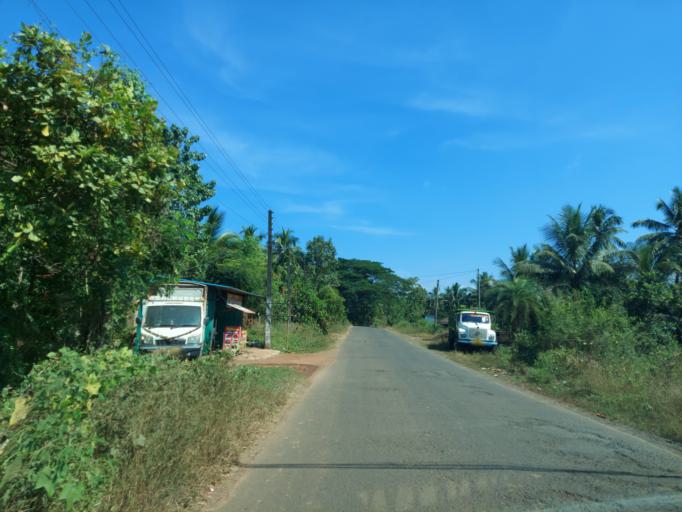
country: IN
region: Maharashtra
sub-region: Sindhudurg
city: Kudal
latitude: 15.9886
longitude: 73.6778
